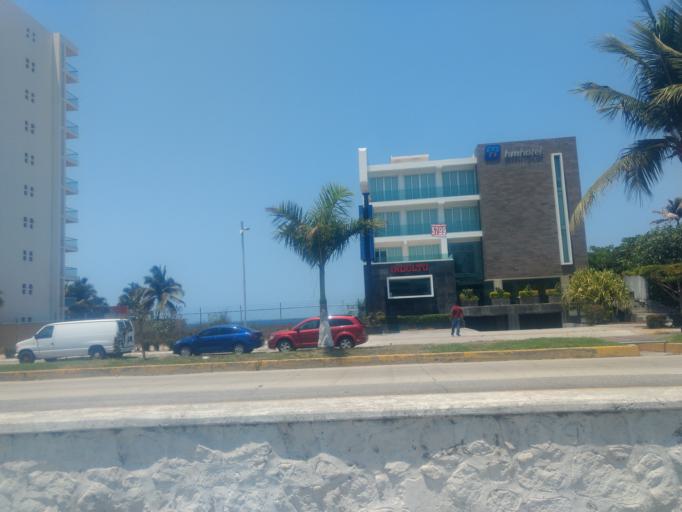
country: MX
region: Colima
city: Tapeixtles
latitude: 19.0884
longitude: -104.3117
